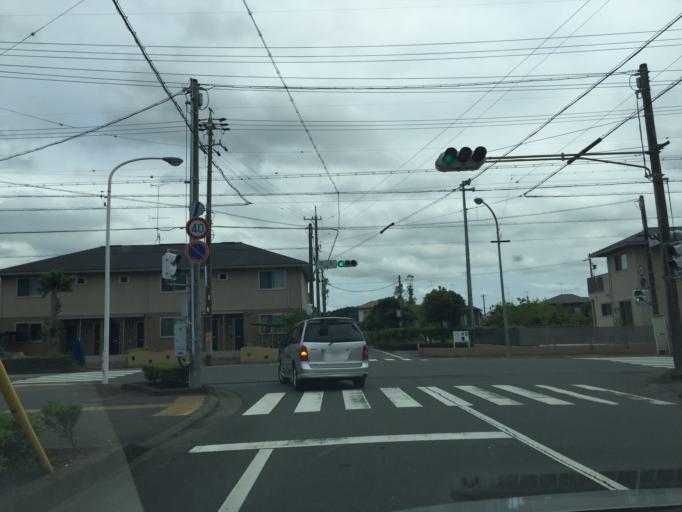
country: JP
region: Shizuoka
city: Fukuroi
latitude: 34.7486
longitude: 137.9304
